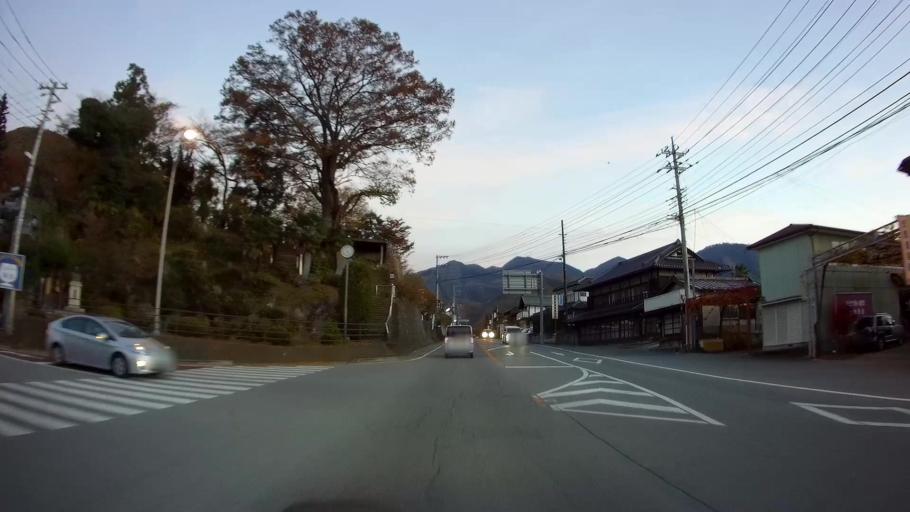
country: JP
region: Yamanashi
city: Enzan
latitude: 35.6602
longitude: 138.7337
